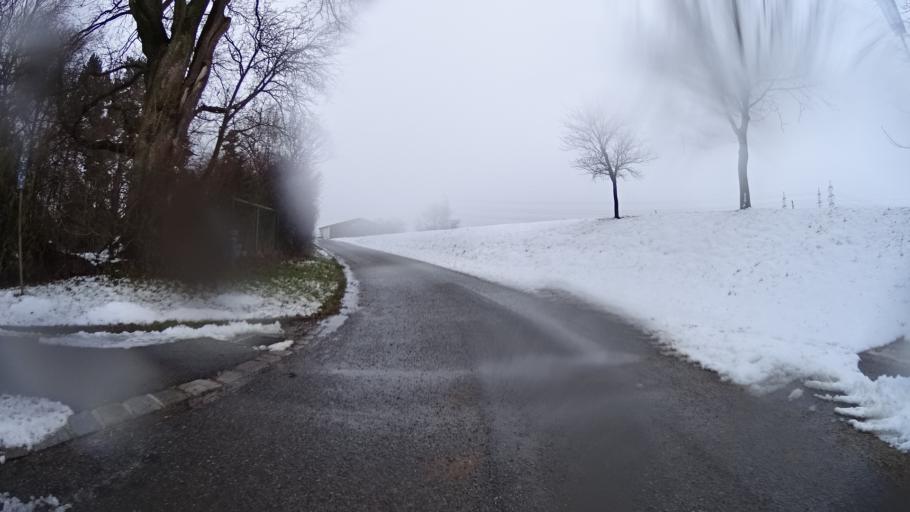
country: AT
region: Lower Austria
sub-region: Politischer Bezirk Korneuburg
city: Spillern
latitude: 48.4043
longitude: 16.2784
